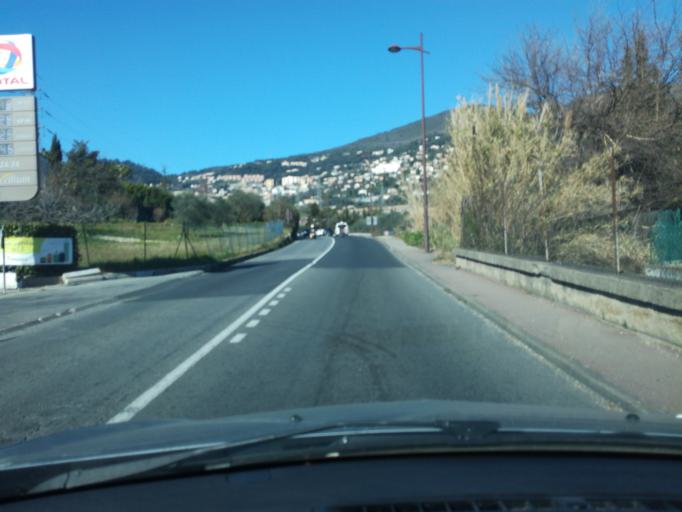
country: FR
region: Provence-Alpes-Cote d'Azur
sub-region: Departement des Alpes-Maritimes
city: Grasse
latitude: 43.6542
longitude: 6.9436
